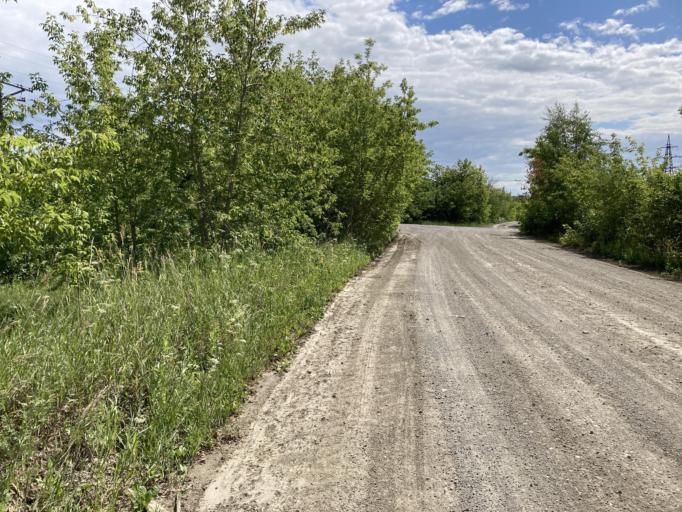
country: RU
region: Sverdlovsk
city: Bogdanovich
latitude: 56.7833
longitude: 62.0646
